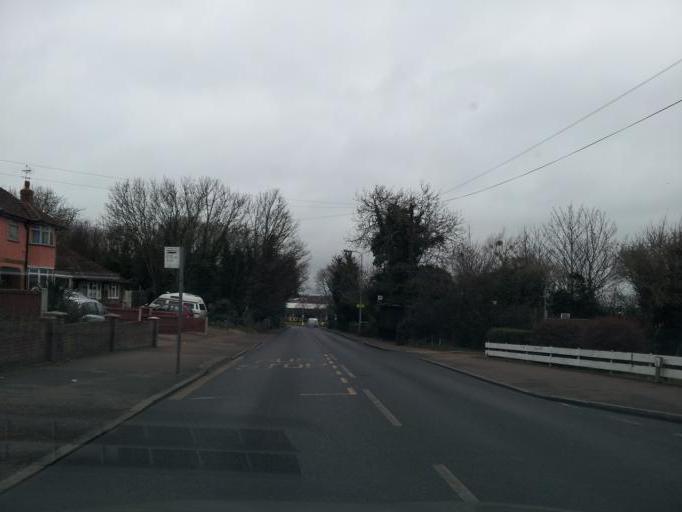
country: GB
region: England
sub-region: Essex
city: Dovercourt
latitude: 51.9376
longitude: 1.2578
